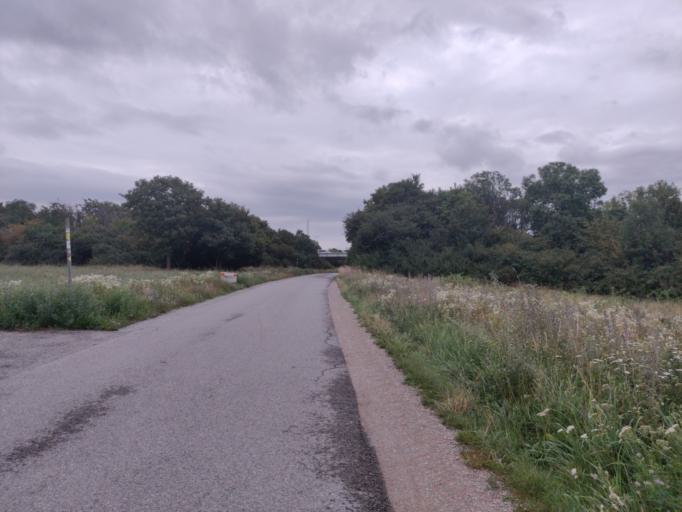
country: AT
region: Vienna
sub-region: Wien Stadt
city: Vienna
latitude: 48.2565
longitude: 16.3788
